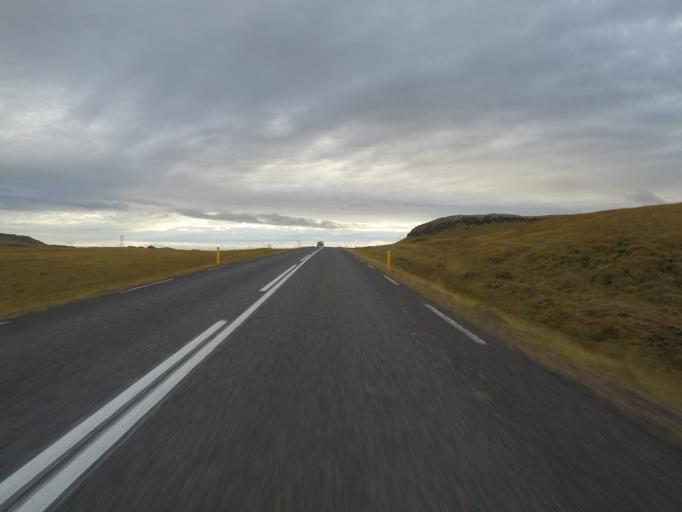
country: IS
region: South
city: Vestmannaeyjar
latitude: 64.0545
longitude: -20.1336
